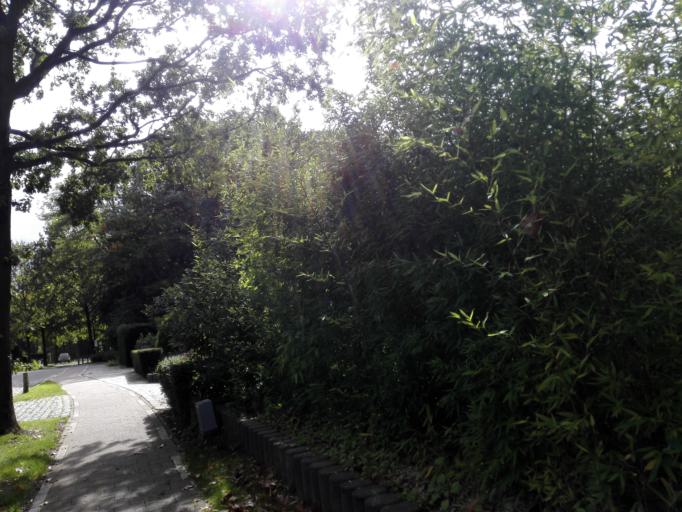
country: BE
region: Flanders
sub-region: Provincie Vlaams-Brabant
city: Oud-Heverlee
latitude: 50.8544
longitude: 4.6811
